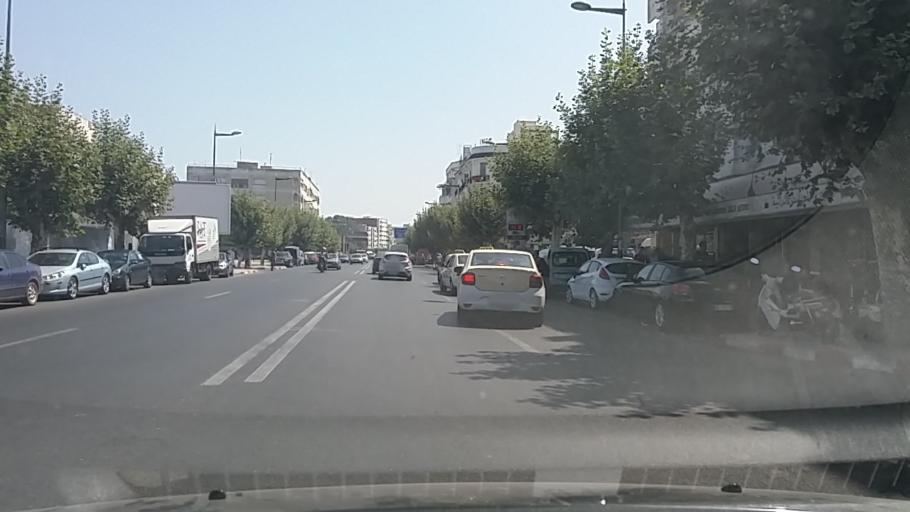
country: MA
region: Gharb-Chrarda-Beni Hssen
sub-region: Kenitra Province
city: Kenitra
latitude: 34.2611
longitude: -6.5806
